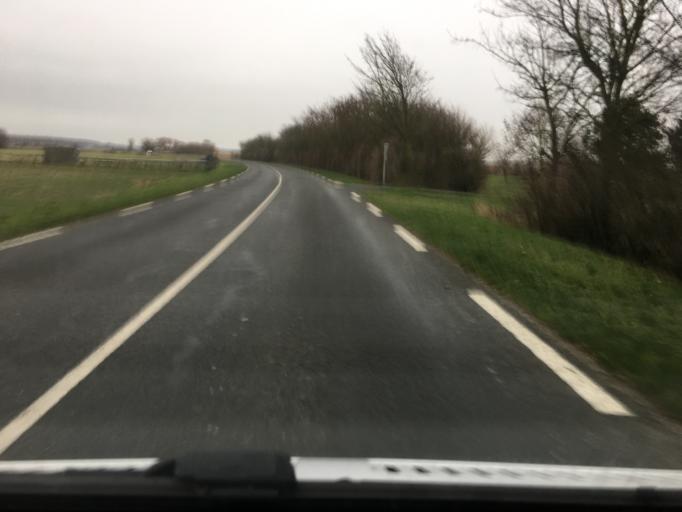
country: FR
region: Picardie
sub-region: Departement de la Somme
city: Pende
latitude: 50.1915
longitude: 1.5617
